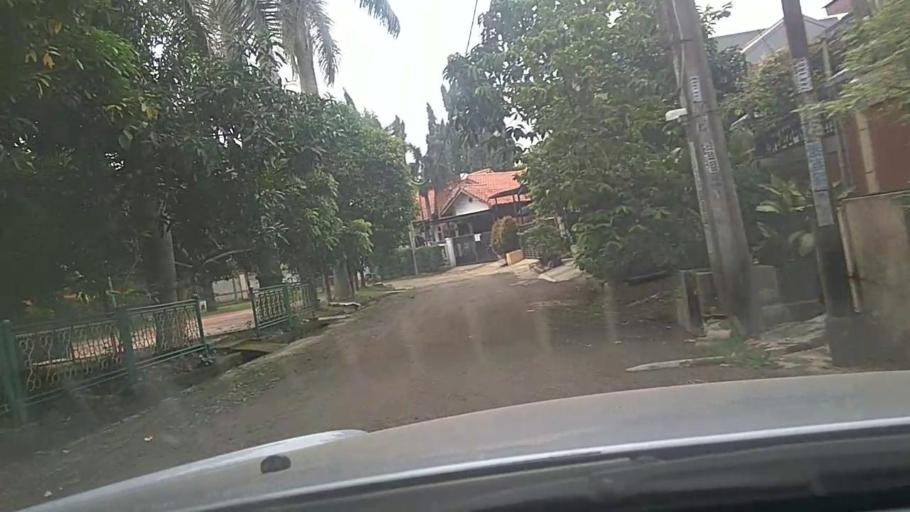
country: ID
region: West Java
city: Pamulang
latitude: -6.3446
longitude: 106.7334
